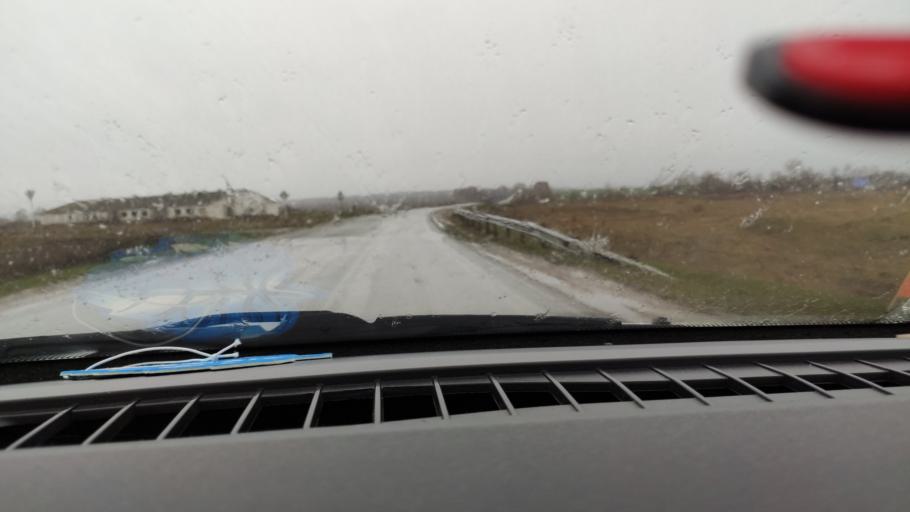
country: RU
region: Samara
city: Chelno-Vershiny
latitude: 54.6862
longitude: 51.1044
